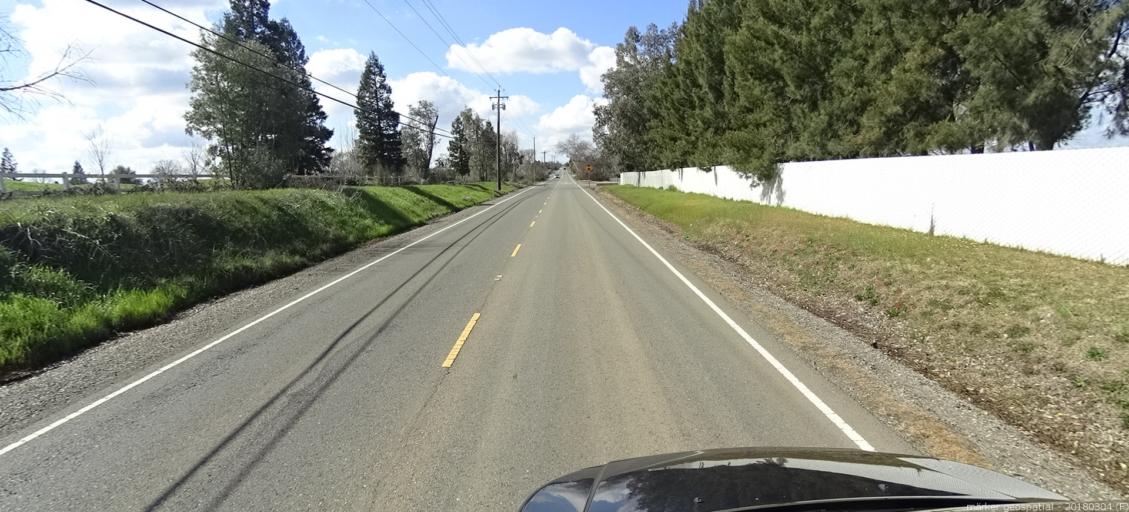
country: US
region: California
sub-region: Sacramento County
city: Vineyard
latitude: 38.4817
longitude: -121.3130
